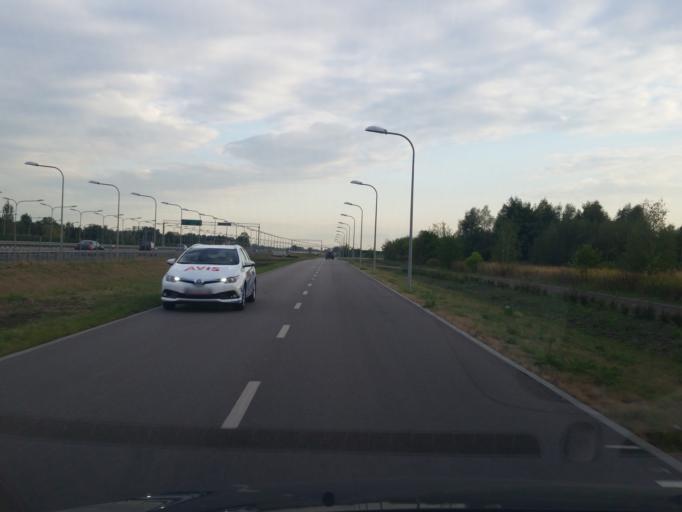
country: PL
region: Masovian Voivodeship
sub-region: Powiat pruszkowski
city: Rybie
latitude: 52.1450
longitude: 20.9880
